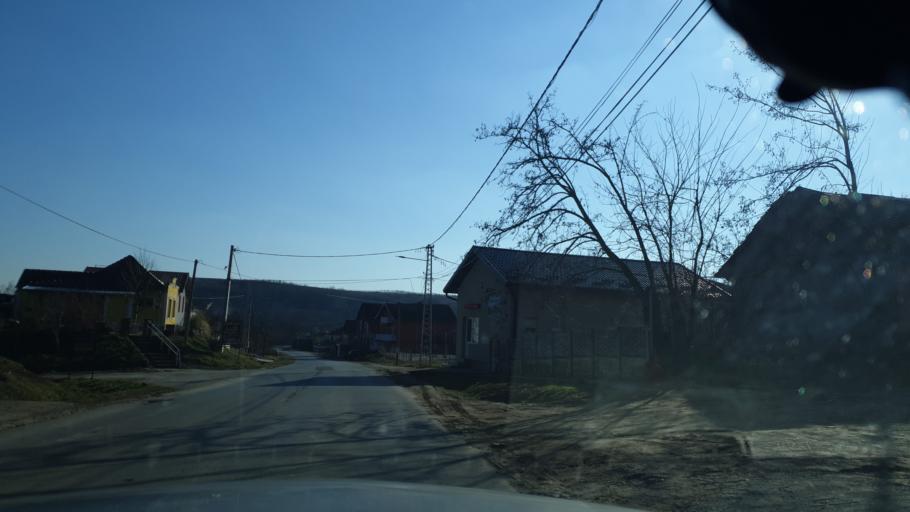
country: RS
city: Vrdnik
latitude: 45.1199
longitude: 19.7939
